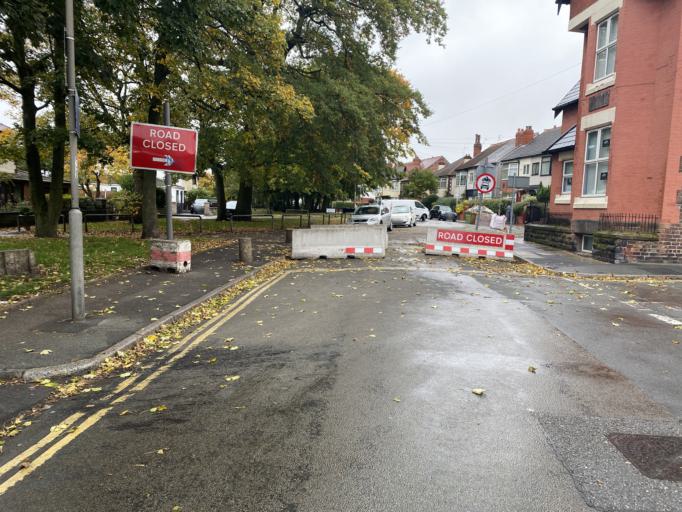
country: GB
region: England
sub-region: Liverpool
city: Liverpool
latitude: 53.4231
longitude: -2.9208
